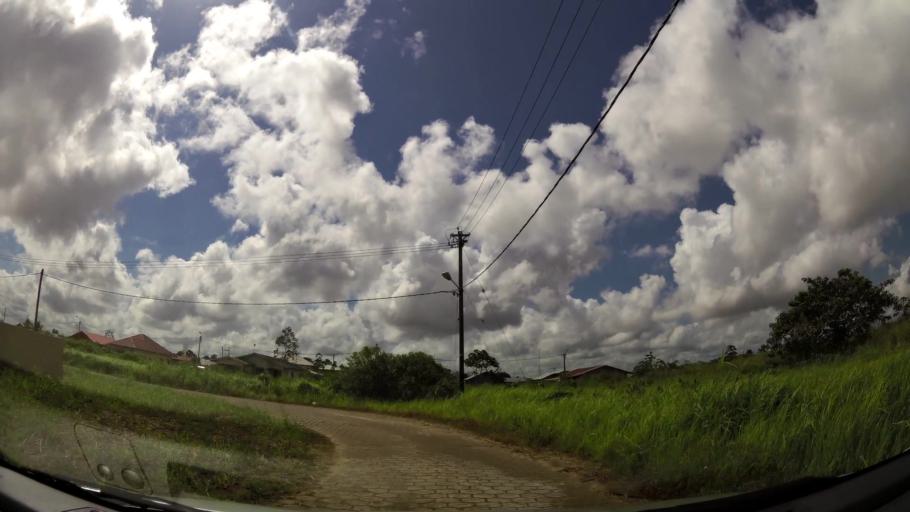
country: SR
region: Paramaribo
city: Paramaribo
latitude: 5.8752
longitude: -55.1283
